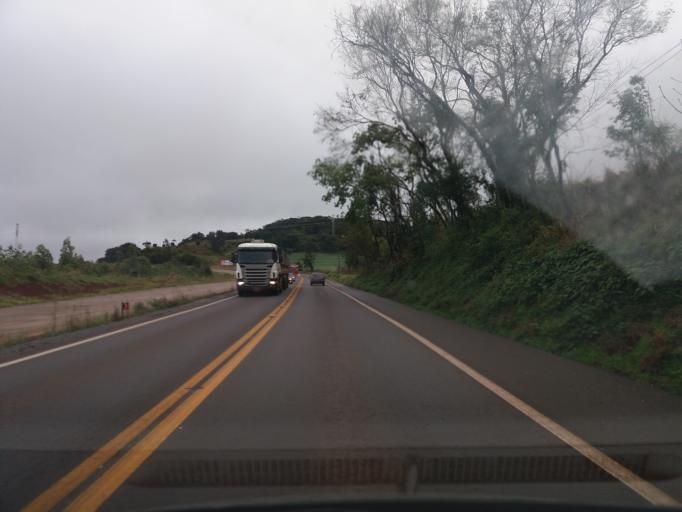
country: BR
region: Parana
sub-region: Cascavel
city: Cascavel
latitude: -25.2434
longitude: -53.5804
